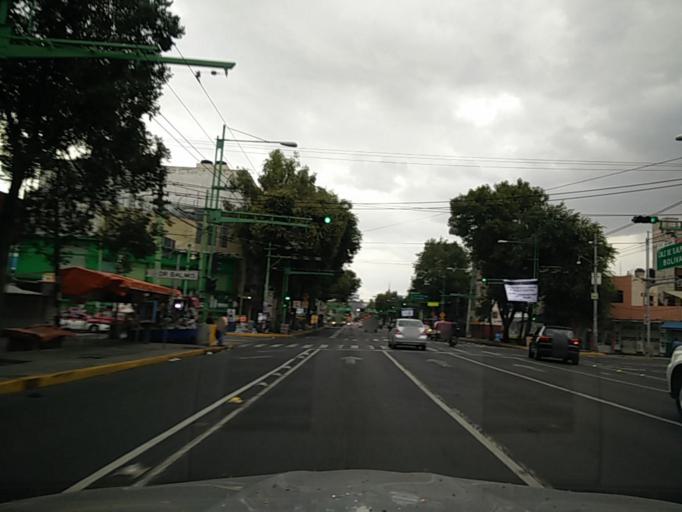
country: MX
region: Mexico City
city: Benito Juarez
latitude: 19.4140
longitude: -99.1440
